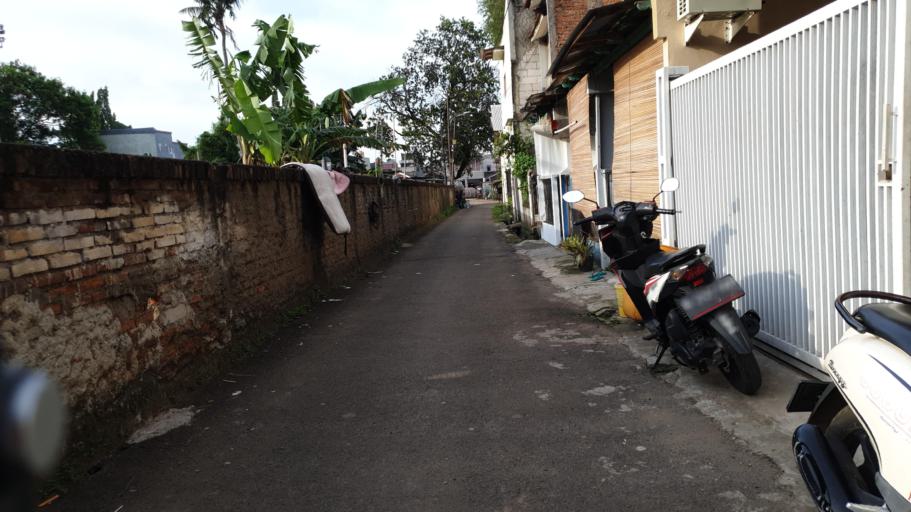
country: ID
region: Banten
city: South Tangerang
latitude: -6.2895
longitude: 106.7893
